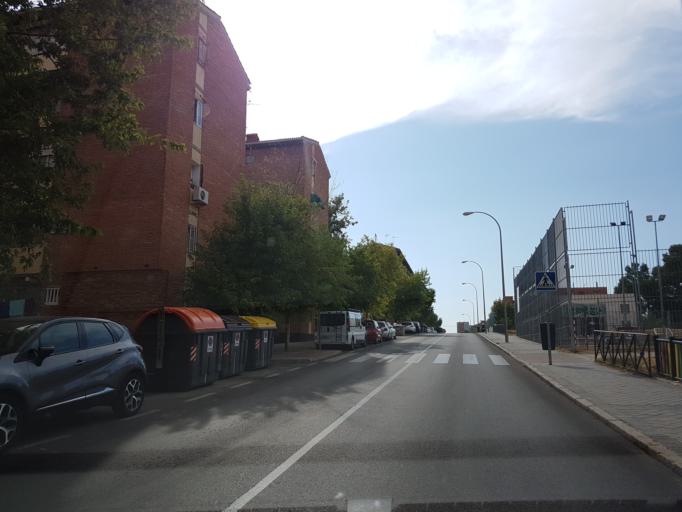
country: ES
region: Madrid
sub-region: Provincia de Madrid
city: Pinar de Chamartin
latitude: 40.4779
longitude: -3.6642
